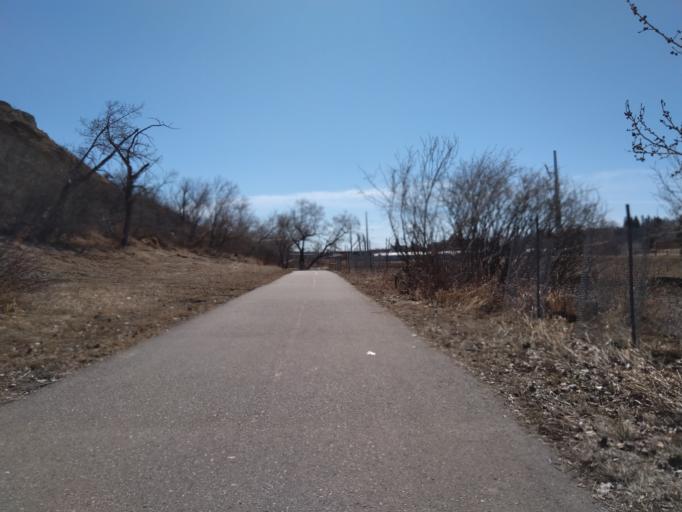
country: CA
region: Alberta
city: Calgary
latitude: 51.0352
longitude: -114.0496
